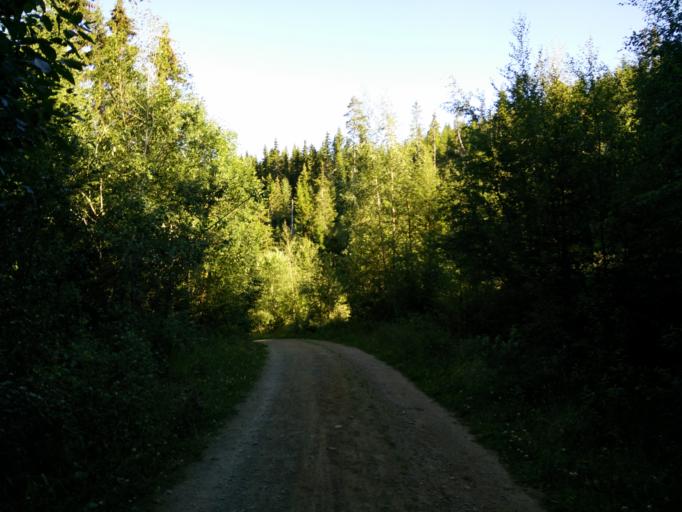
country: NO
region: Sor-Trondelag
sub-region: Skaun
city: Borsa
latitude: 63.3212
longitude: 10.0232
